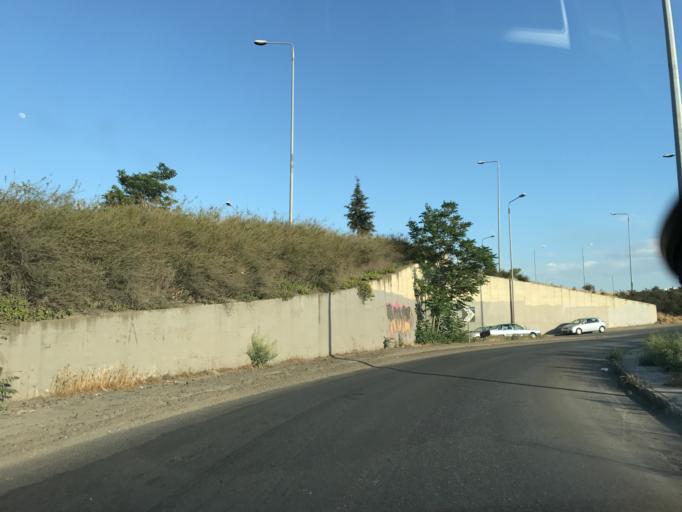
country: GR
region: Central Macedonia
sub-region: Nomos Thessalonikis
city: Menemeni
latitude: 40.6539
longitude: 22.9010
